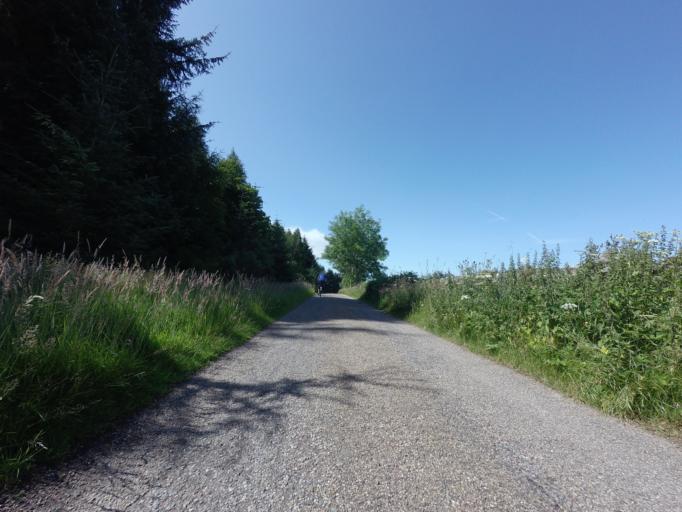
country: GB
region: Scotland
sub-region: Highland
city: Nairn
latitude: 57.5094
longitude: -3.8951
